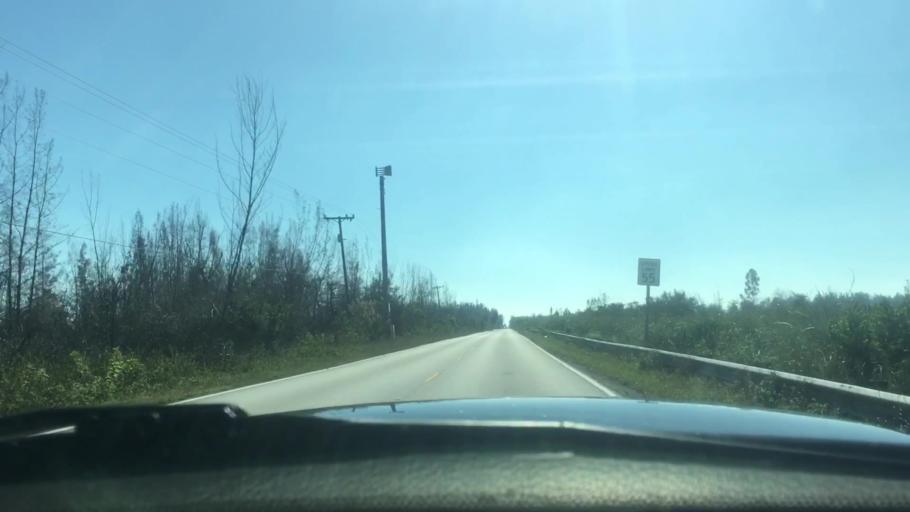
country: US
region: Florida
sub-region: Miami-Dade County
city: Florida City
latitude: 25.4271
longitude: -80.4691
